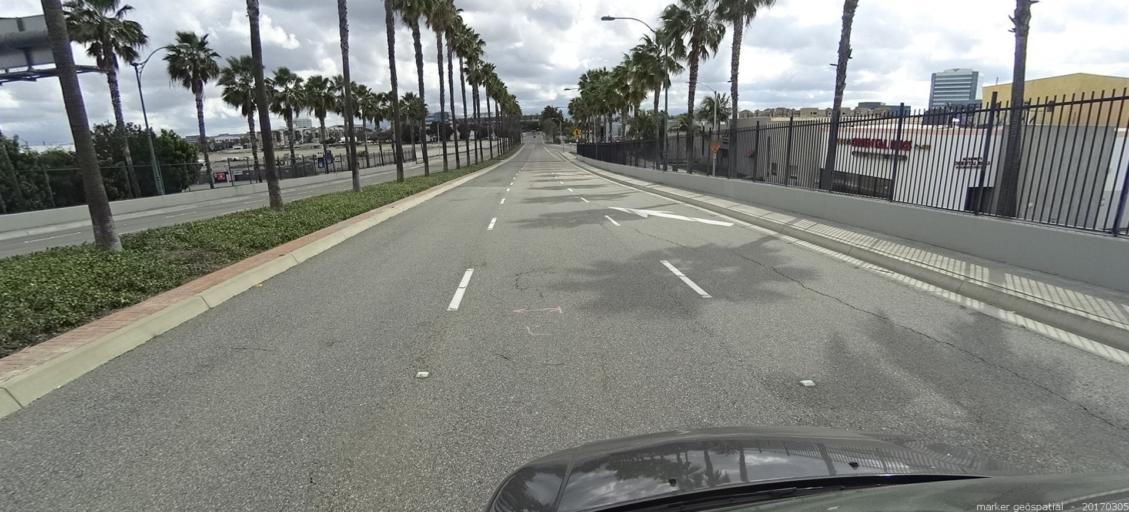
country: US
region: California
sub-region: Orange County
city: Anaheim
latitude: 33.7997
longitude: -117.8959
